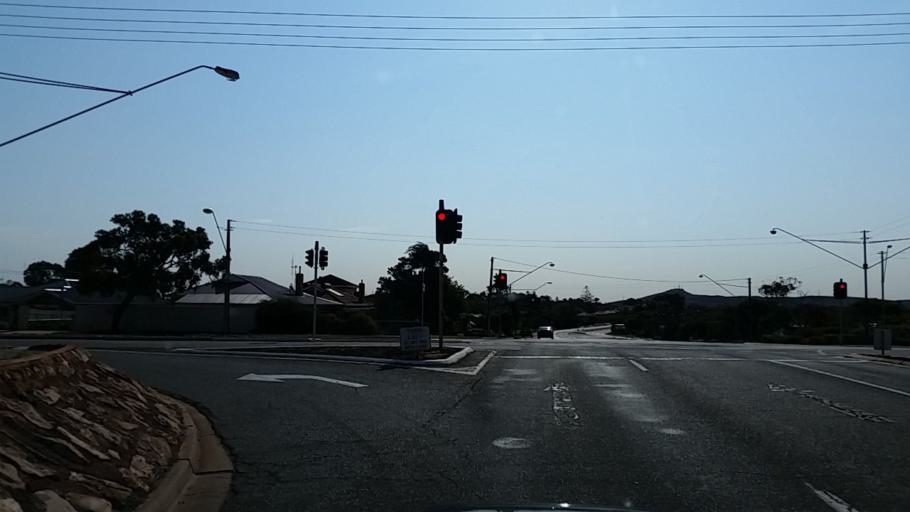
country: AU
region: South Australia
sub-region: Whyalla
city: Whyalla
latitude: -33.0255
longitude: 137.5724
